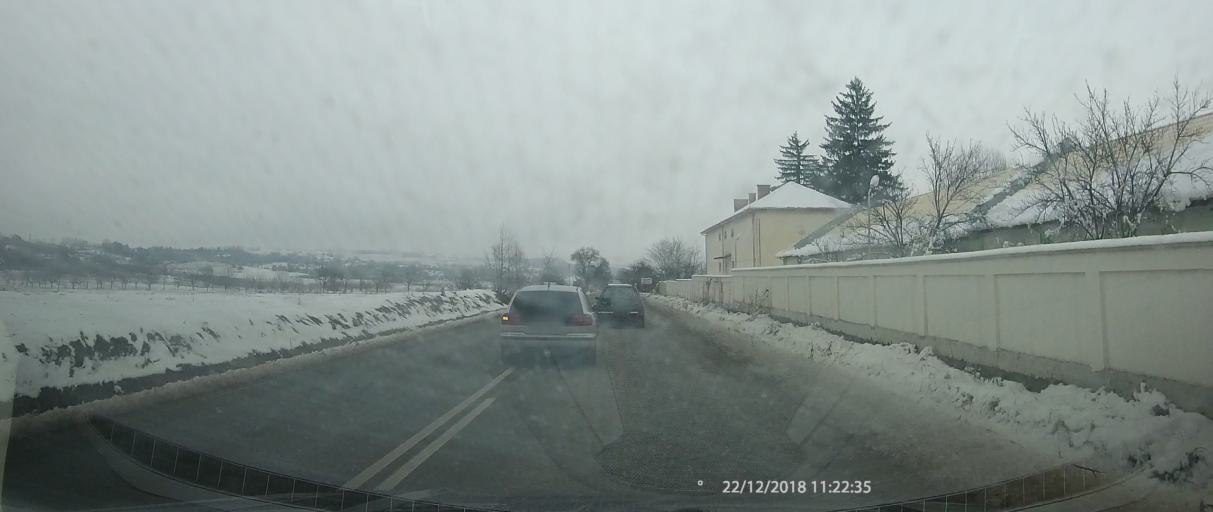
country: BG
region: Kyustendil
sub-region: Obshtina Kyustendil
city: Kyustendil
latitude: 42.2577
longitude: 22.8592
